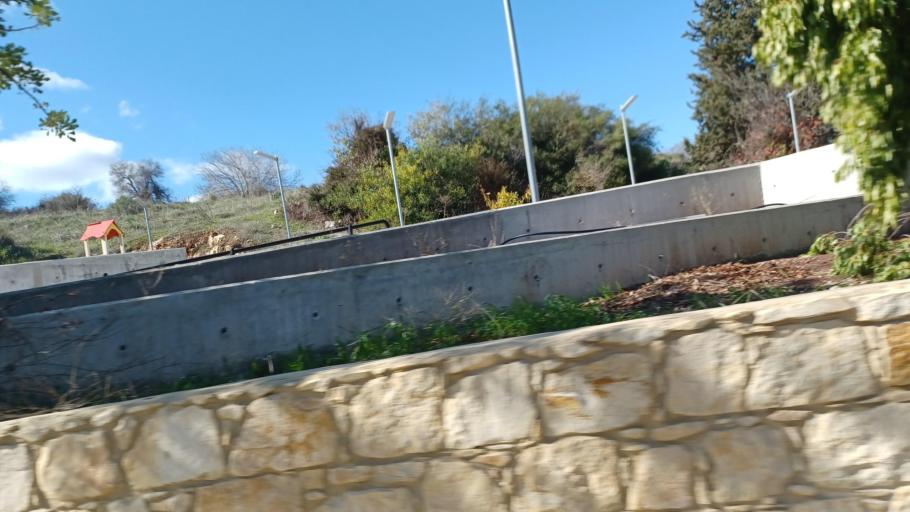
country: CY
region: Pafos
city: Polis
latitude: 34.9660
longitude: 32.4232
